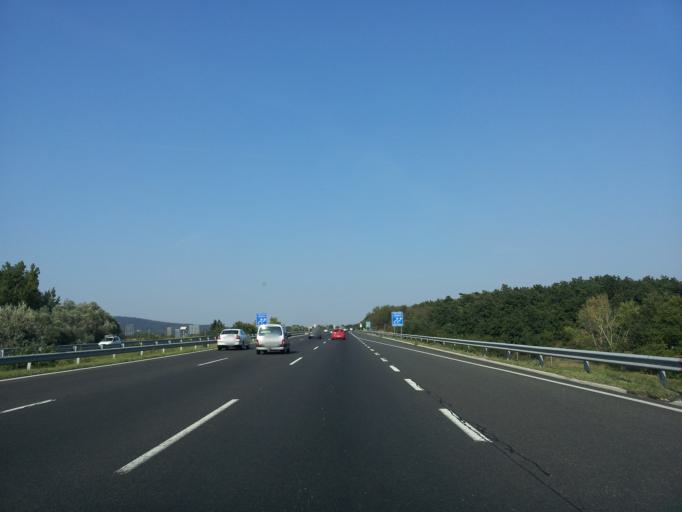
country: HU
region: Fejer
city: Pakozd
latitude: 47.2262
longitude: 18.5731
